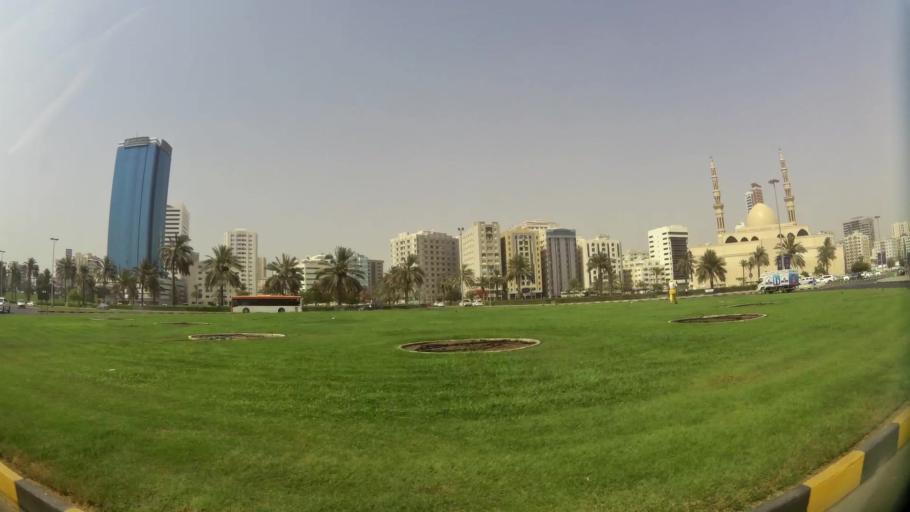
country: AE
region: Ash Shariqah
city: Sharjah
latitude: 25.3494
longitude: 55.3851
